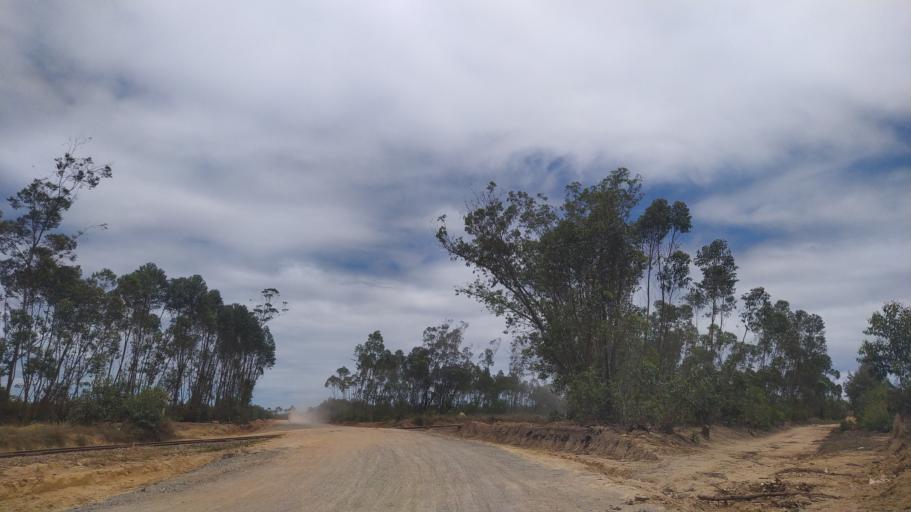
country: MG
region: Alaotra Mangoro
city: Moramanga
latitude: -18.5904
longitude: 48.2765
